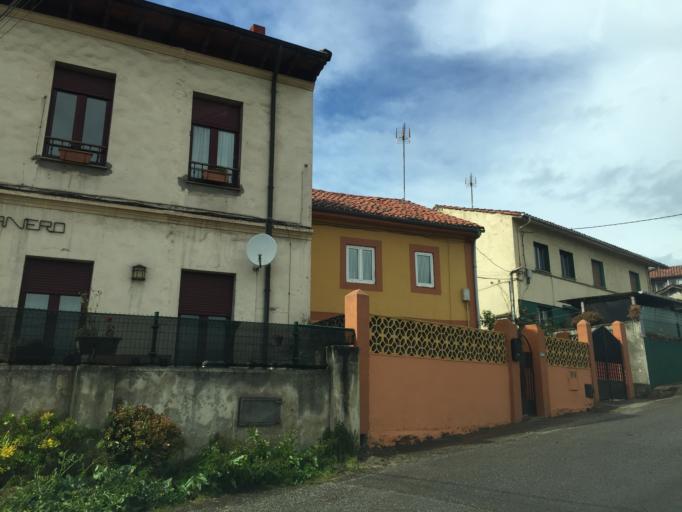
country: ES
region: Asturias
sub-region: Province of Asturias
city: Natahoyo
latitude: 43.5516
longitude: -5.7066
